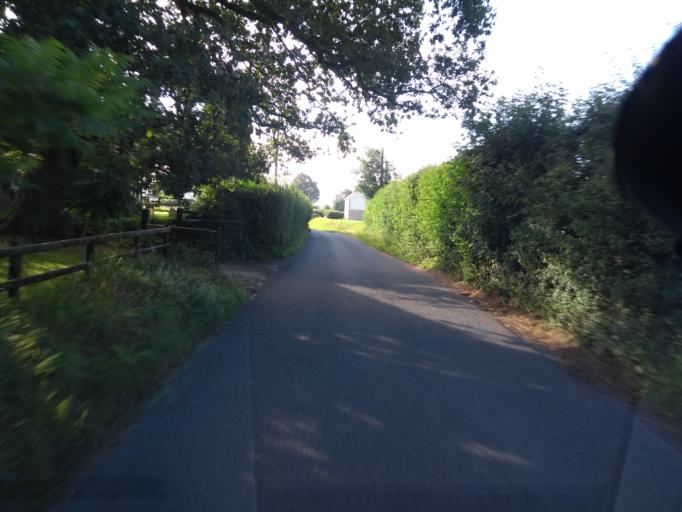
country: GB
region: England
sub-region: Somerset
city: South Petherton
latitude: 50.9583
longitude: -2.8016
